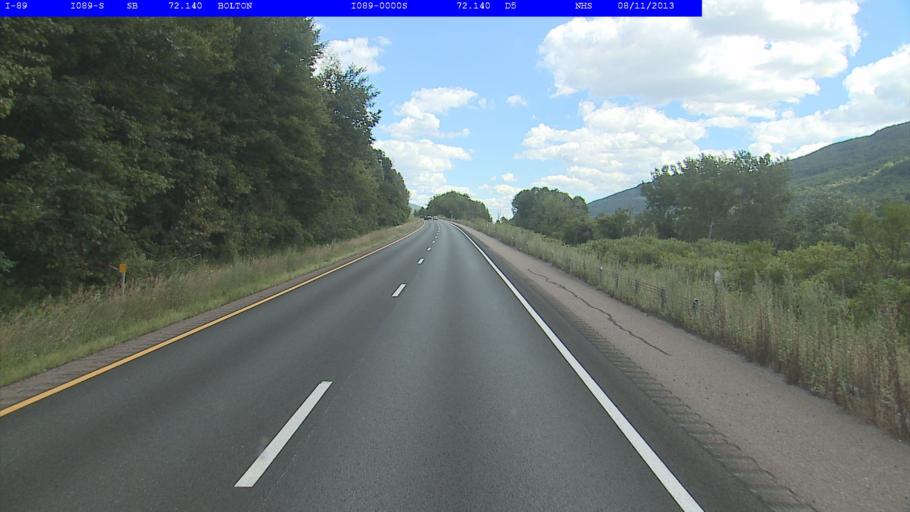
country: US
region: Vermont
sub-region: Chittenden County
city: Jericho
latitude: 44.3791
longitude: -72.9092
